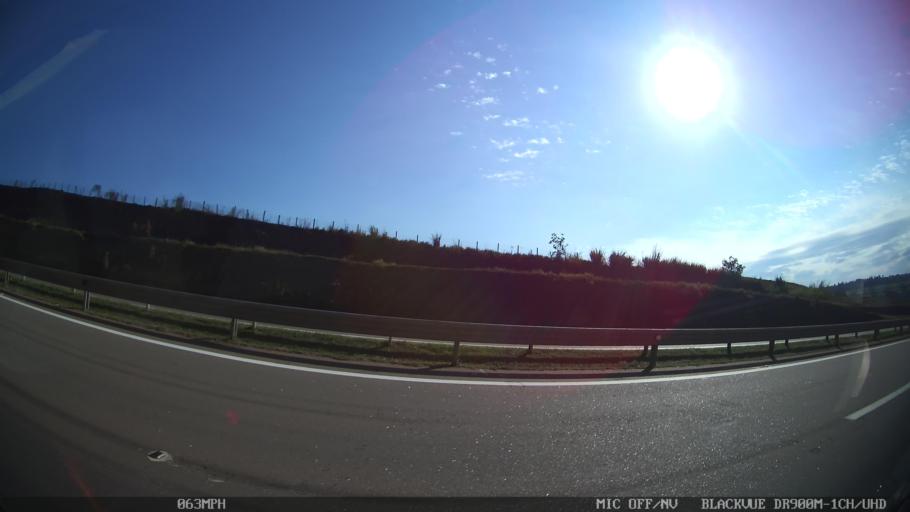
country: BR
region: Sao Paulo
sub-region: Piracicaba
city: Piracicaba
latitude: -22.7069
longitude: -47.6116
